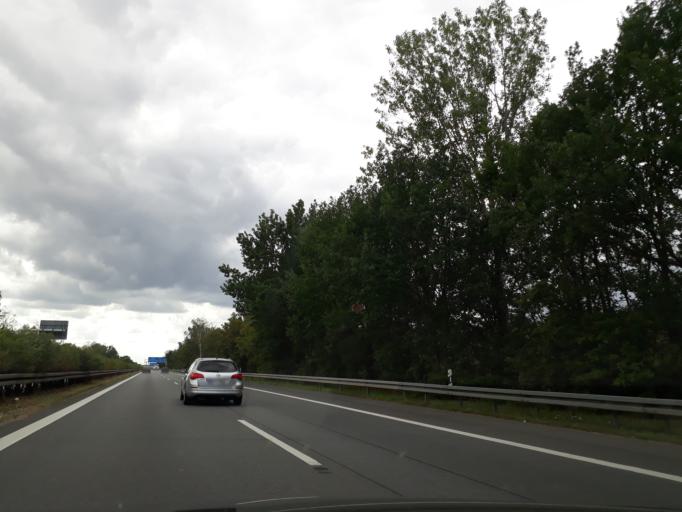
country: DE
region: Brandenburg
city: Bernau bei Berlin
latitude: 52.6401
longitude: 13.5667
